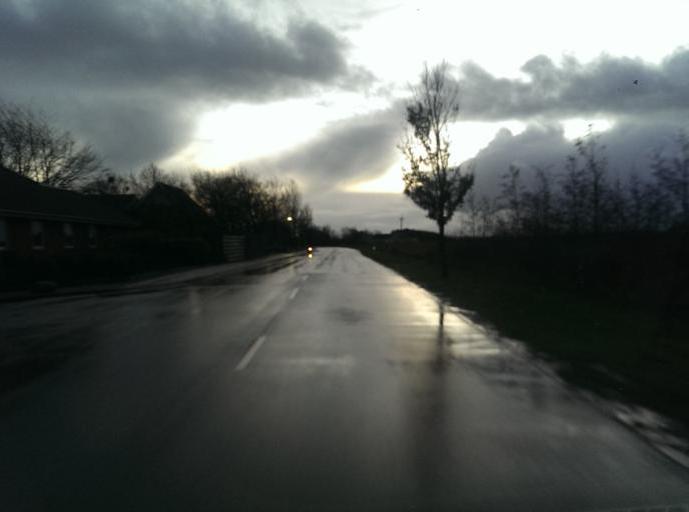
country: DK
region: South Denmark
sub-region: Esbjerg Kommune
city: Bramming
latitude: 55.4621
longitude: 8.6953
